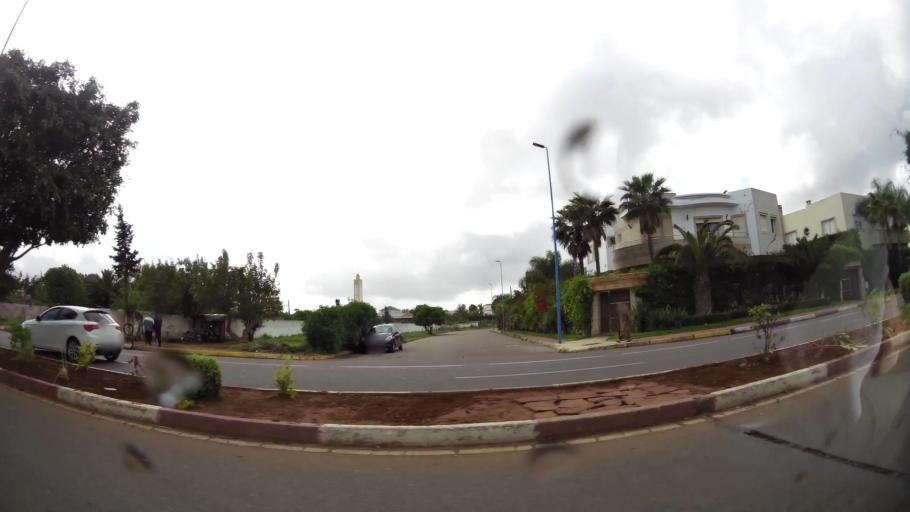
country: MA
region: Grand Casablanca
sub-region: Casablanca
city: Casablanca
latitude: 33.5431
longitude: -7.6310
